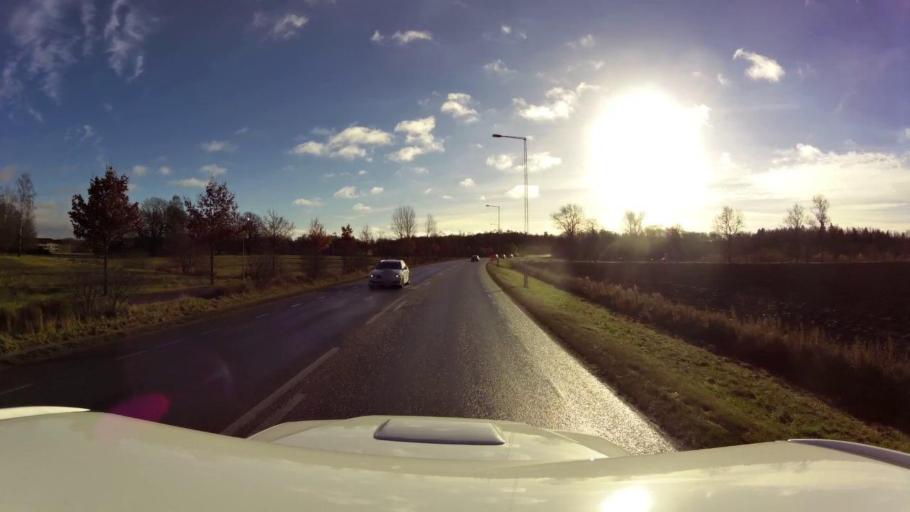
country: SE
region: OEstergoetland
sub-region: Linkopings Kommun
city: Linkoping
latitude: 58.3884
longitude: 15.6273
